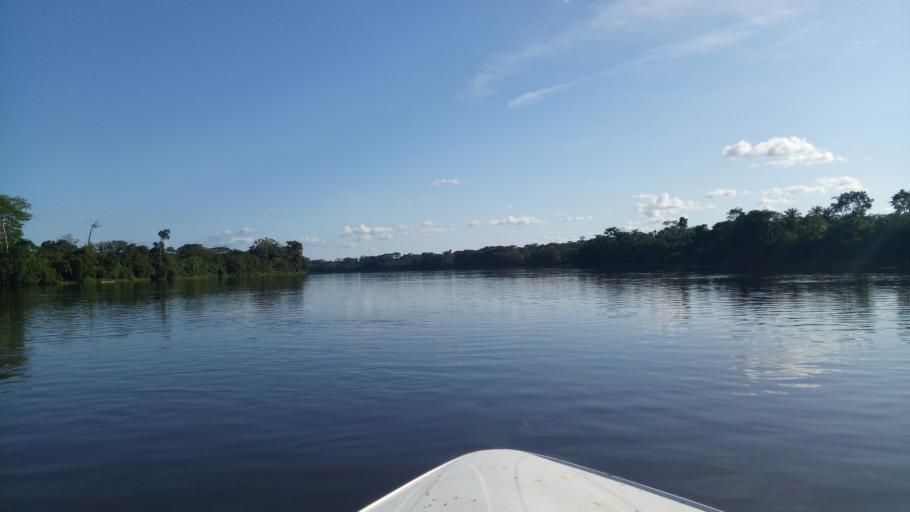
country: CD
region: Eastern Province
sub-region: Sous-Region de la Tshopo
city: Yangambi
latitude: 0.3431
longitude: 24.1329
